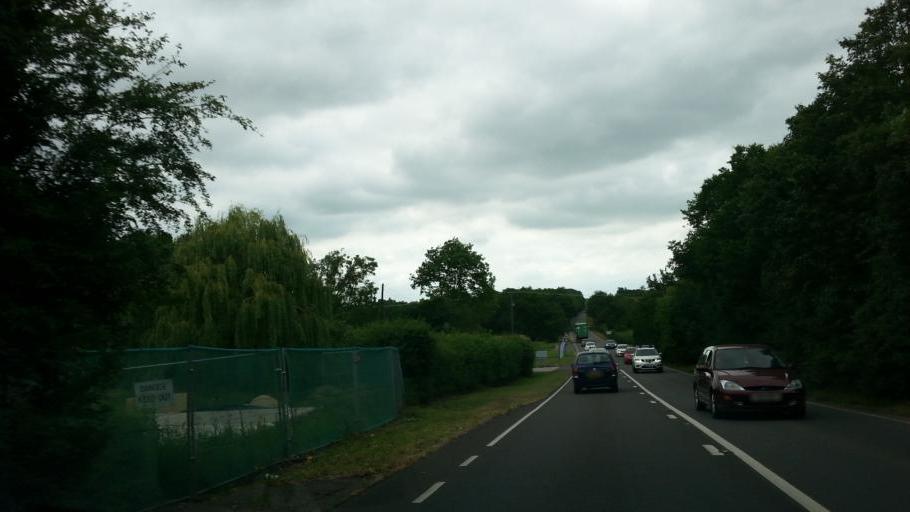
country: GB
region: England
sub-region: Cambridgeshire
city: Papworth Everard
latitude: 52.2809
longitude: -0.1409
